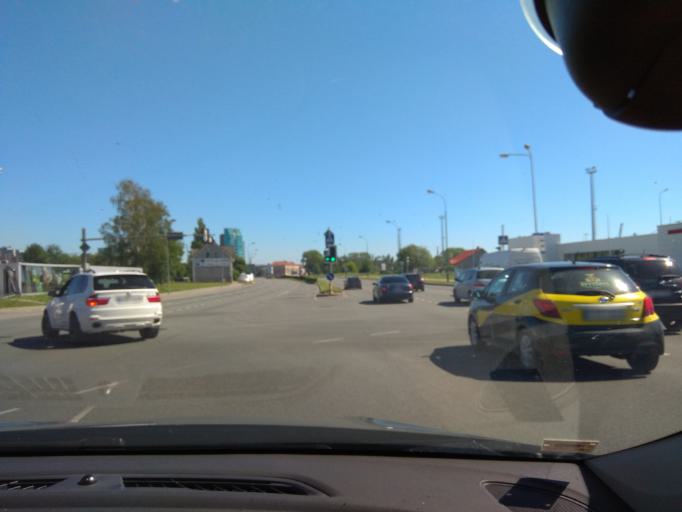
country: LT
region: Klaipedos apskritis
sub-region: Klaipeda
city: Klaipeda
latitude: 55.6874
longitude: 21.1459
